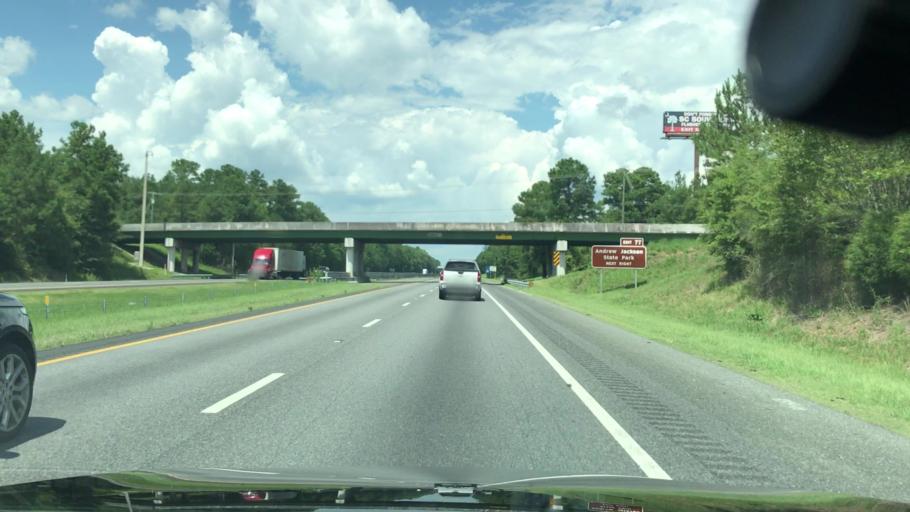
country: US
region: South Carolina
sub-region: York County
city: Lesslie
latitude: 34.9039
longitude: -80.9871
